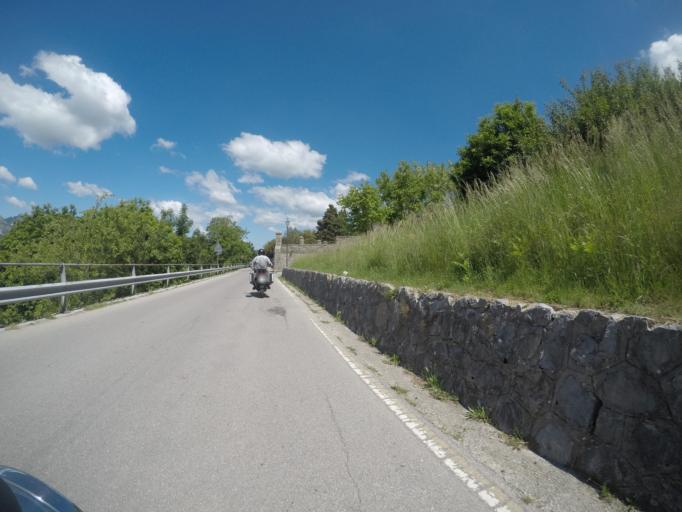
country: IT
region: Tuscany
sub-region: Provincia di Lucca
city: Careggine
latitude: 44.1188
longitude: 10.3276
